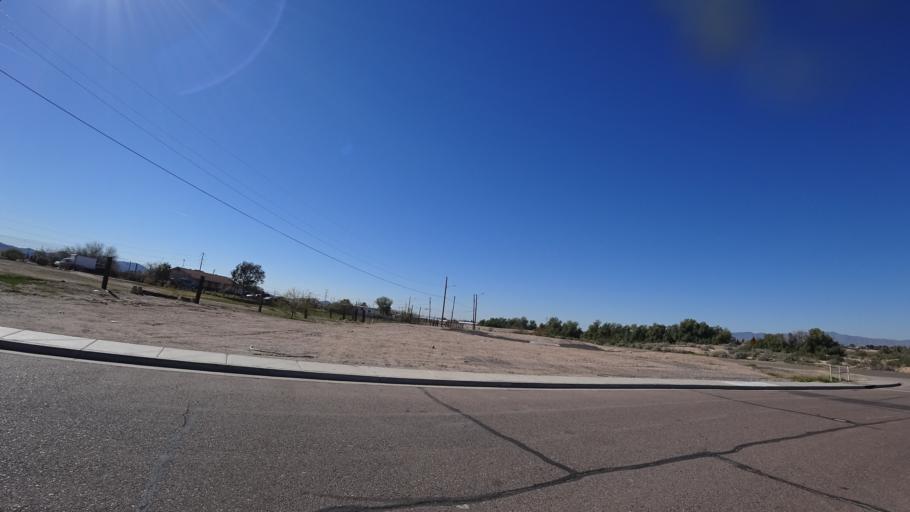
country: US
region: Arizona
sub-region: Maricopa County
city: Avondale
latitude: 33.4135
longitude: -112.3348
